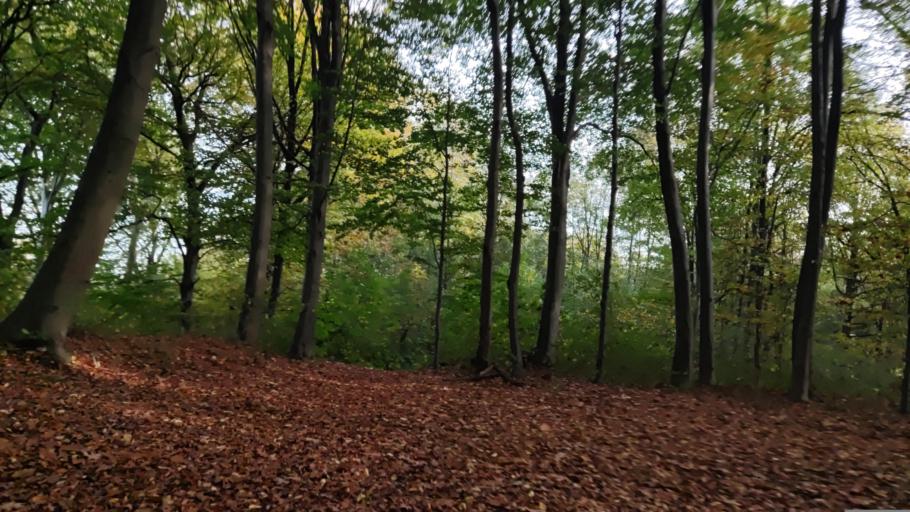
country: DE
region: North Rhine-Westphalia
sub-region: Regierungsbezirk Arnsberg
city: Herne
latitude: 51.5233
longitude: 7.2519
